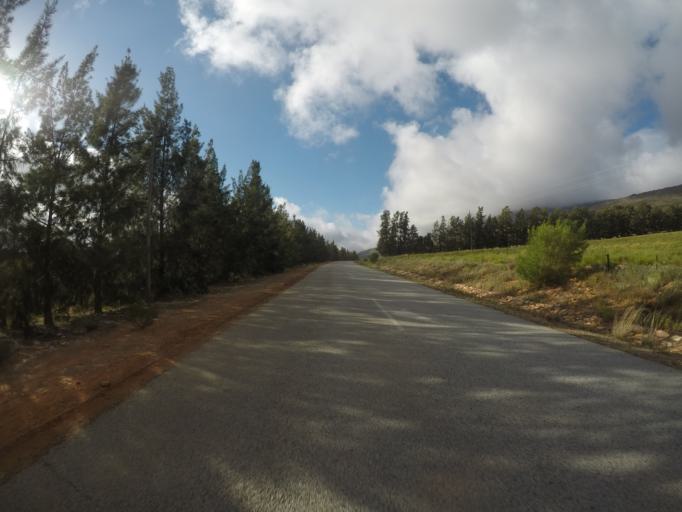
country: ZA
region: Western Cape
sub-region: West Coast District Municipality
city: Clanwilliam
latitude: -32.3496
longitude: 18.8468
